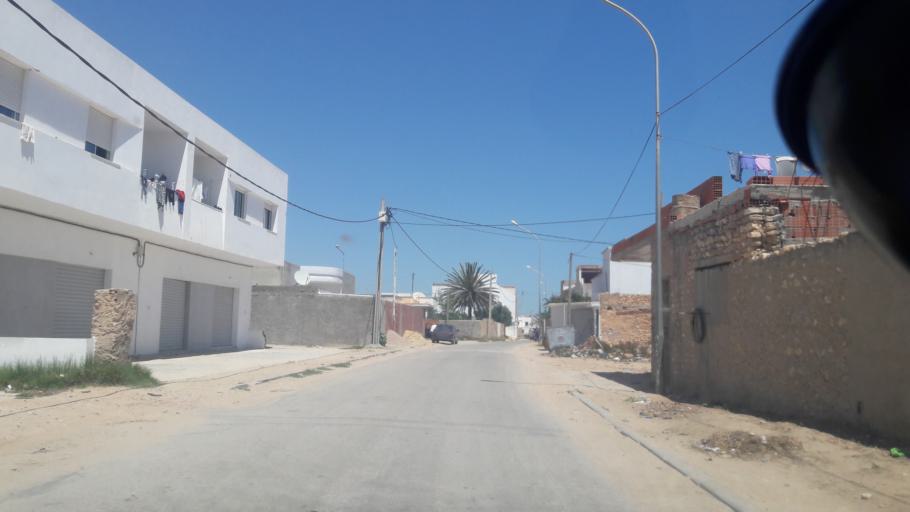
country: TN
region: Safaqis
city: Al Qarmadah
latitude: 34.8060
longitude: 10.7512
